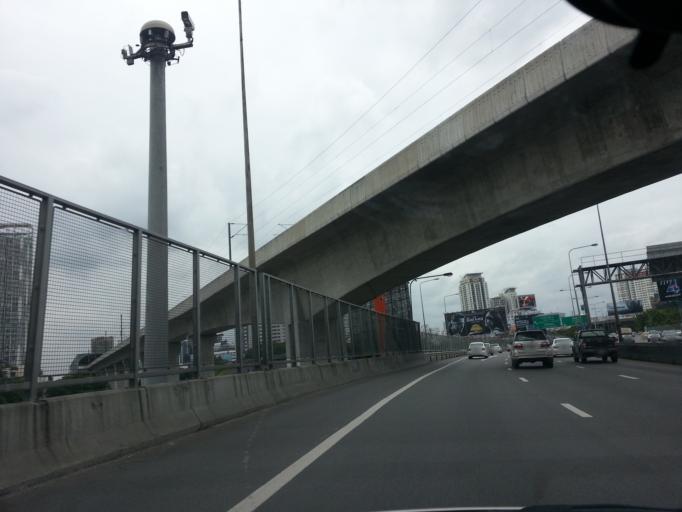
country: TH
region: Bangkok
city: Ratchathewi
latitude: 13.7540
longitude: 100.5463
